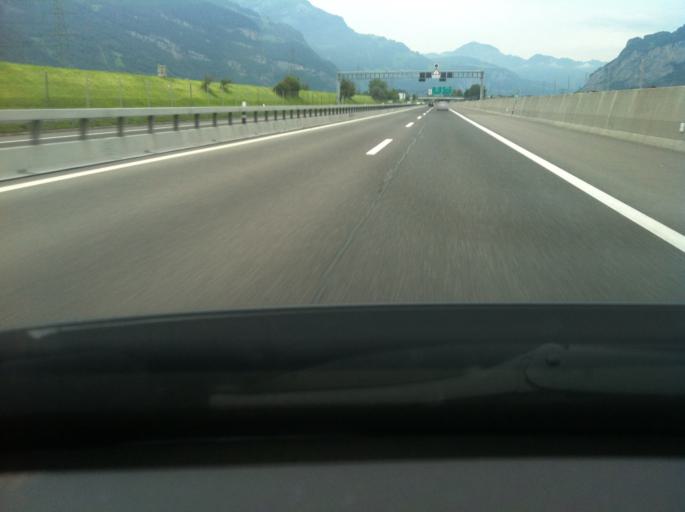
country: CH
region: Uri
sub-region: Uri
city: Seedorf
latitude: 46.8808
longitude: 8.6233
